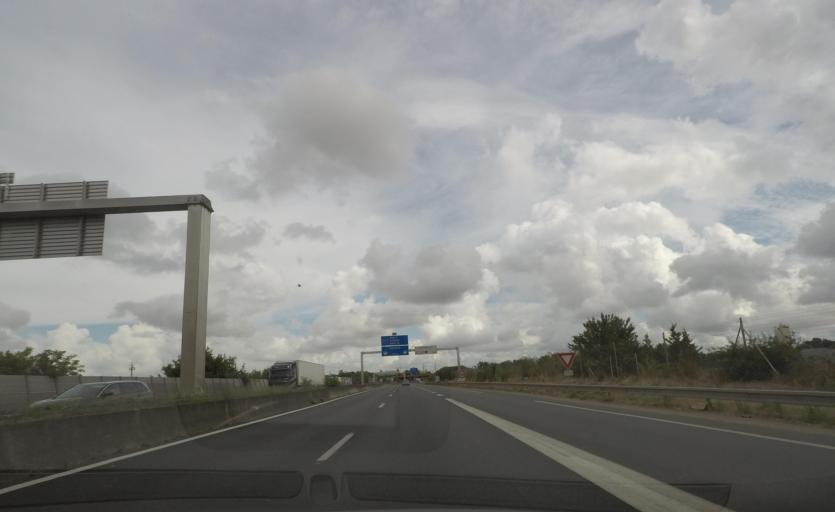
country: FR
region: Pays de la Loire
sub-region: Departement de Maine-et-Loire
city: Angers
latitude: 47.4628
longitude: -0.5169
